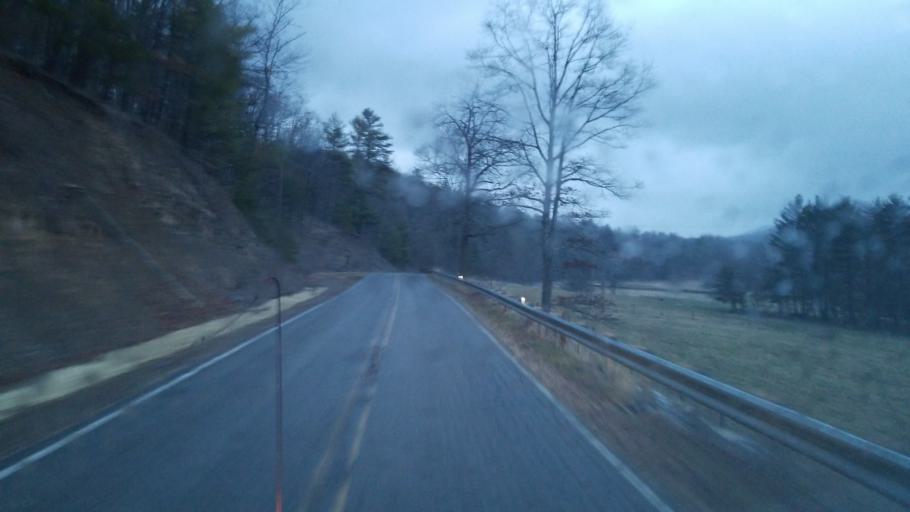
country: US
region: Virginia
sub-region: Pulaski County
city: Pulaski
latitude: 37.1120
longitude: -80.8863
